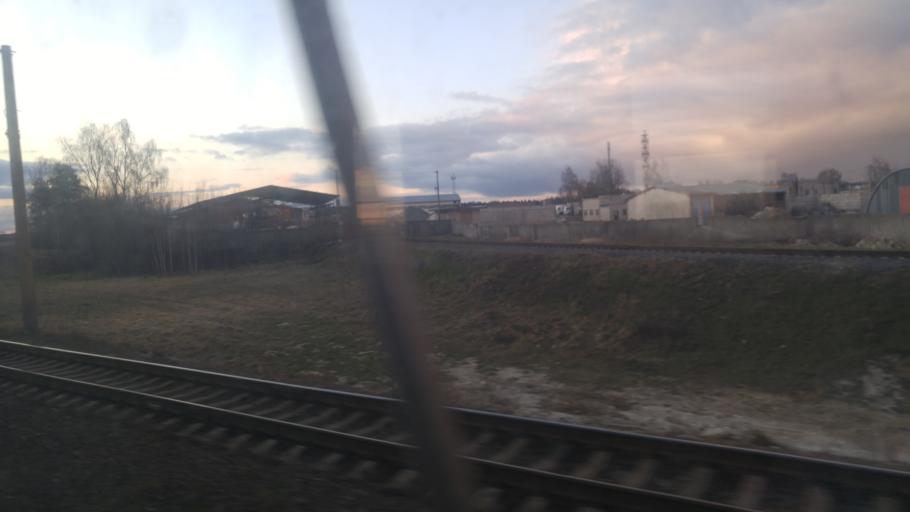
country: BY
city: Michanovichi
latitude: 53.7535
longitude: 27.6782
